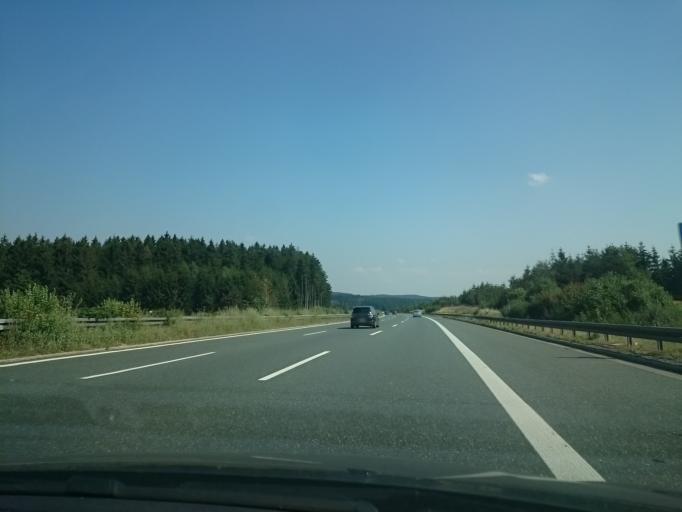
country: DE
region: Bavaria
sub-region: Upper Franconia
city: Leupoldsgrun
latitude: 50.2472
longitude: 11.7883
